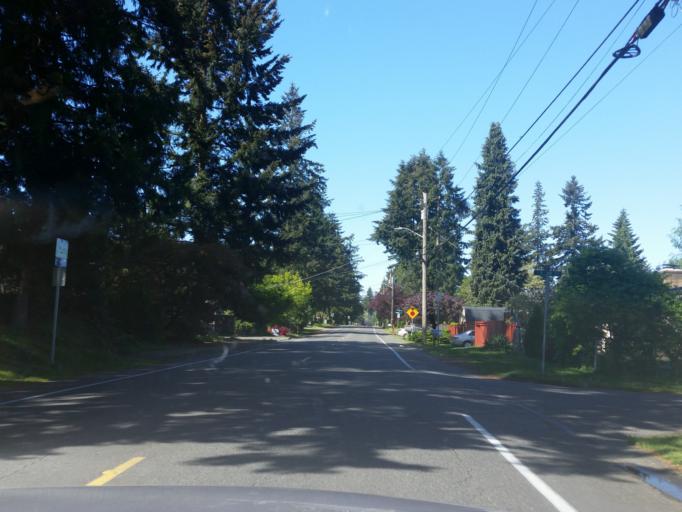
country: US
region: Washington
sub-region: Snohomish County
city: Esperance
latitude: 47.7721
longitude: -122.3513
